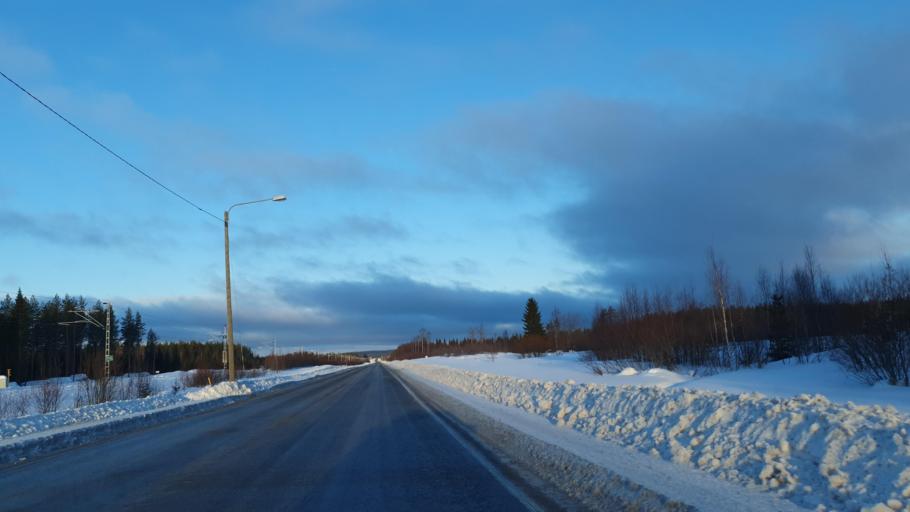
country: FI
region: Kainuu
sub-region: Kajaani
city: Paltamo
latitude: 64.4022
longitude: 27.7932
